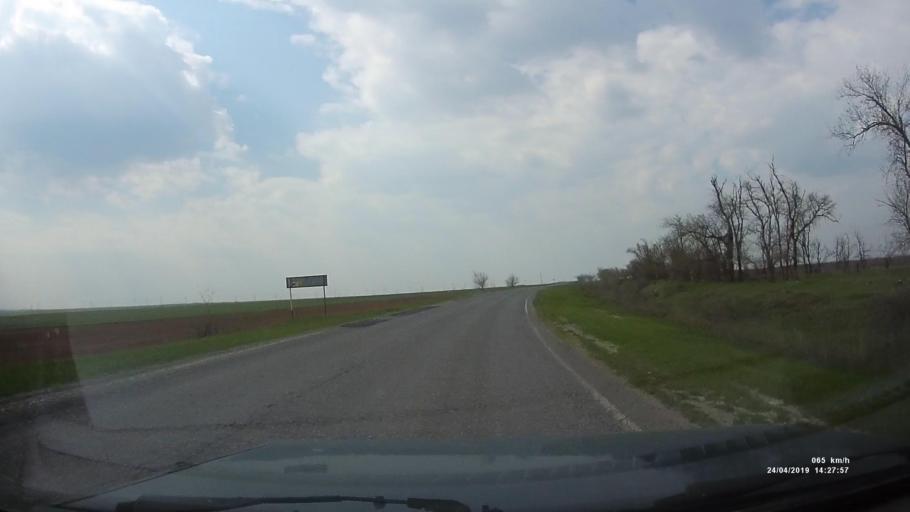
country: RU
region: Kalmykiya
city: Arshan'
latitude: 46.3348
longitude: 44.0344
